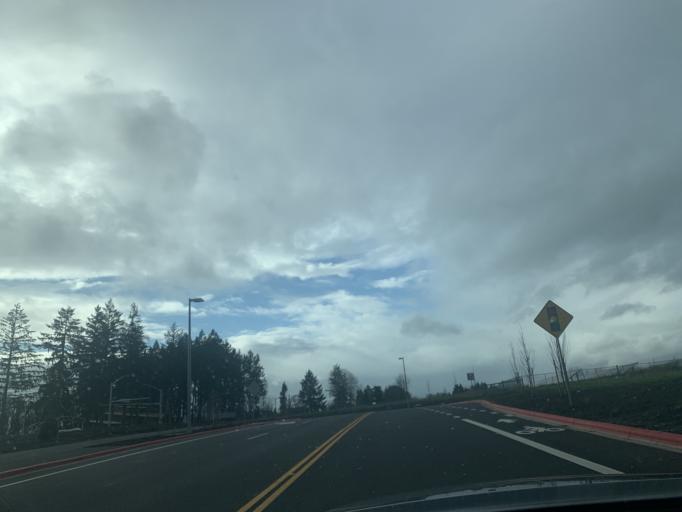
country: US
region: Oregon
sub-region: Washington County
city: Bethany
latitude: 45.5638
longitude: -122.8596
